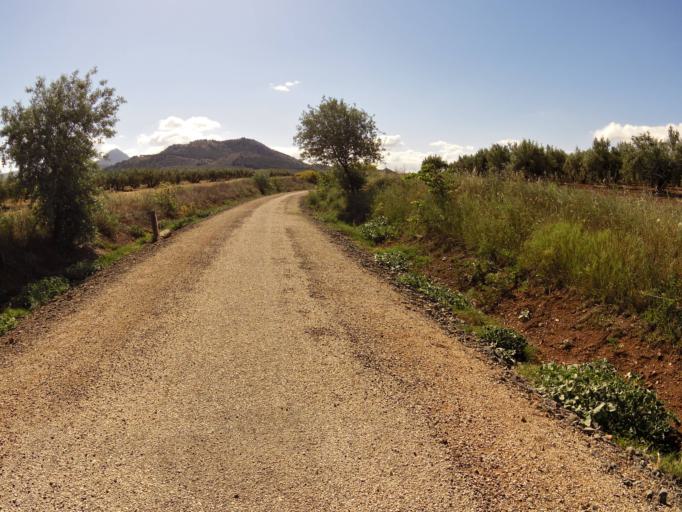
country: ES
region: Andalusia
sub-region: Provincia de Jaen
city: Alcaudete
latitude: 37.6030
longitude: -4.1454
